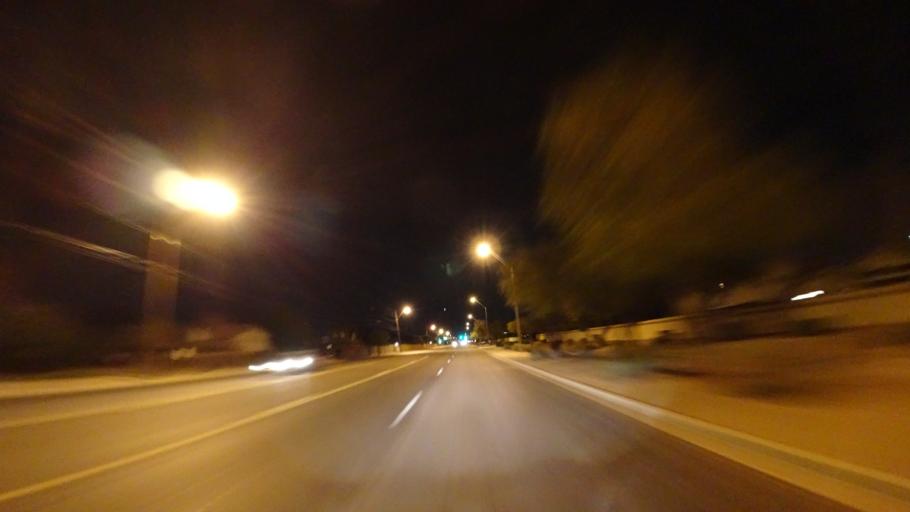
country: US
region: Arizona
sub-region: Maricopa County
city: Gilbert
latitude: 33.3500
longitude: -111.7946
